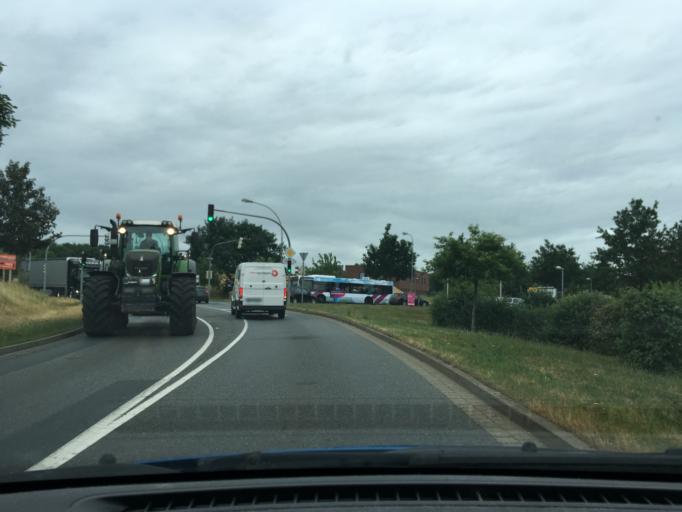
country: DE
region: Lower Saxony
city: Harmstorf
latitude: 53.3907
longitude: 10.0391
